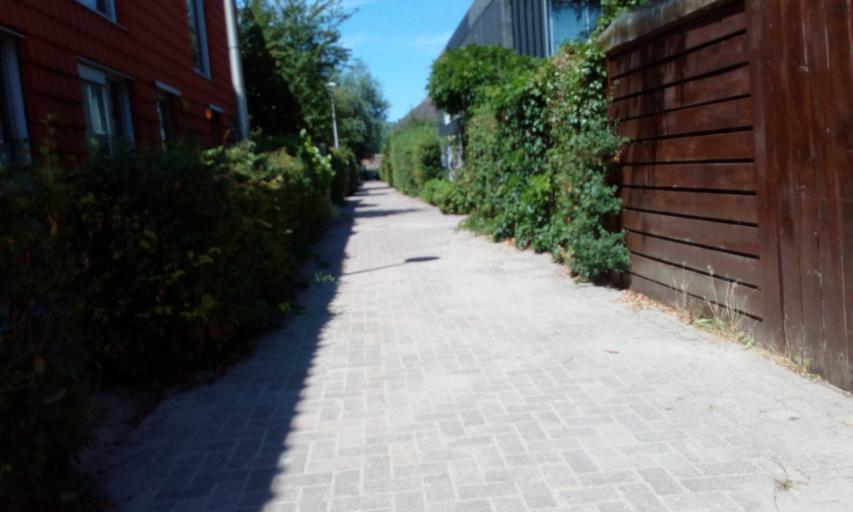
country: NL
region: South Holland
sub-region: Gemeente Den Haag
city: Ypenburg
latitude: 52.0346
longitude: 4.3699
